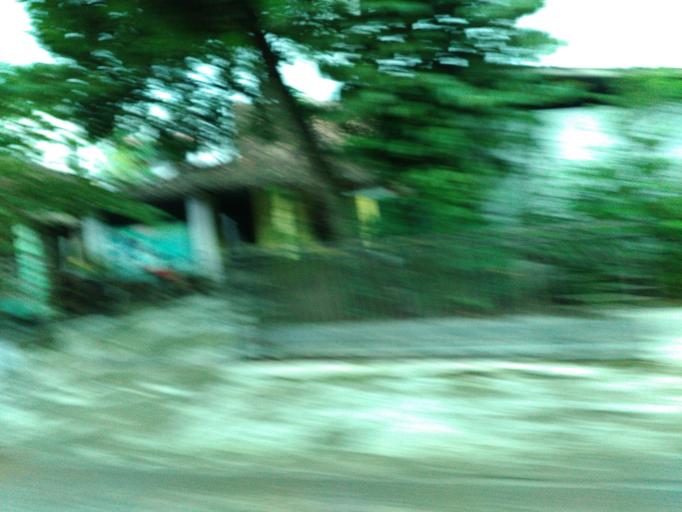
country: ID
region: Central Java
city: Ceper
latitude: -7.6549
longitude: 110.6924
